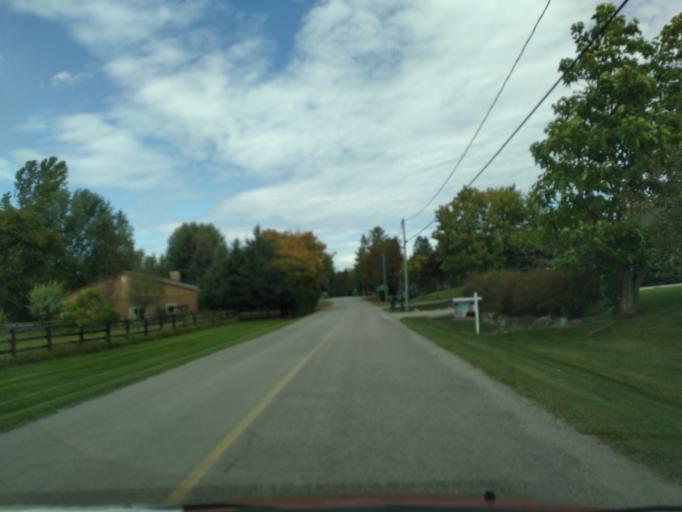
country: CA
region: Ontario
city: Keswick
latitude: 44.2705
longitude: -79.3665
